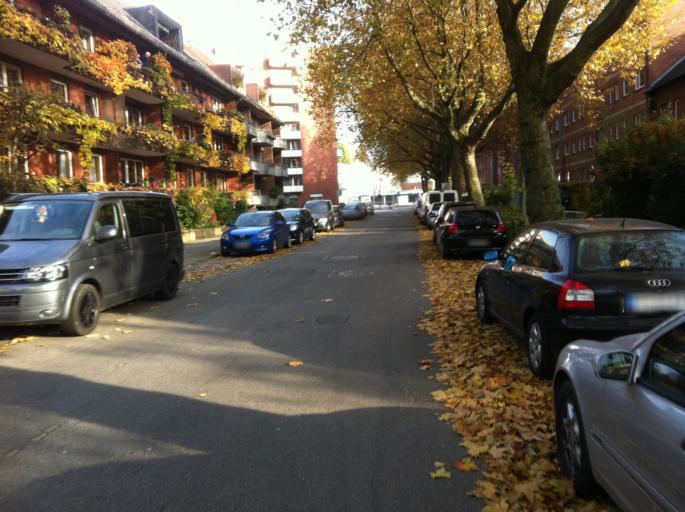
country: DE
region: Hamburg
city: Stellingen
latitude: 53.5720
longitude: 9.9354
